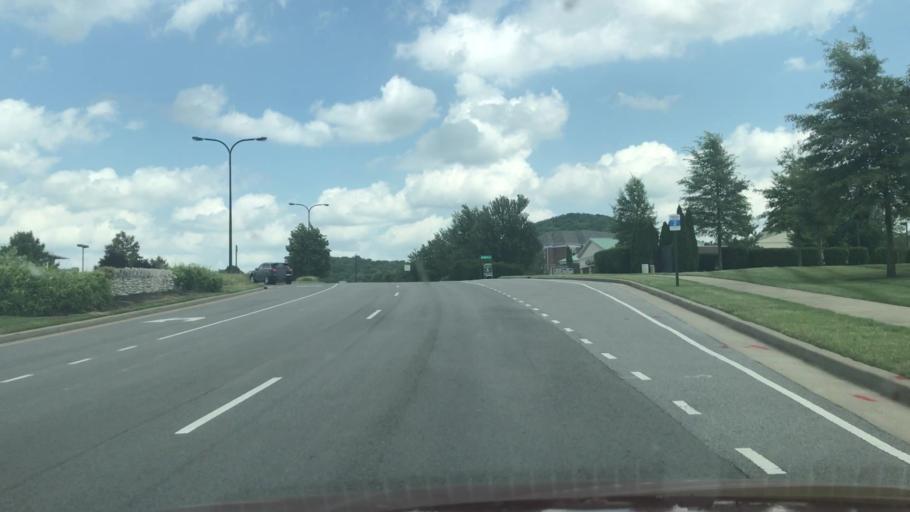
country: US
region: Tennessee
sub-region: Williamson County
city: Brentwood Estates
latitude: 35.9588
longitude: -86.8053
